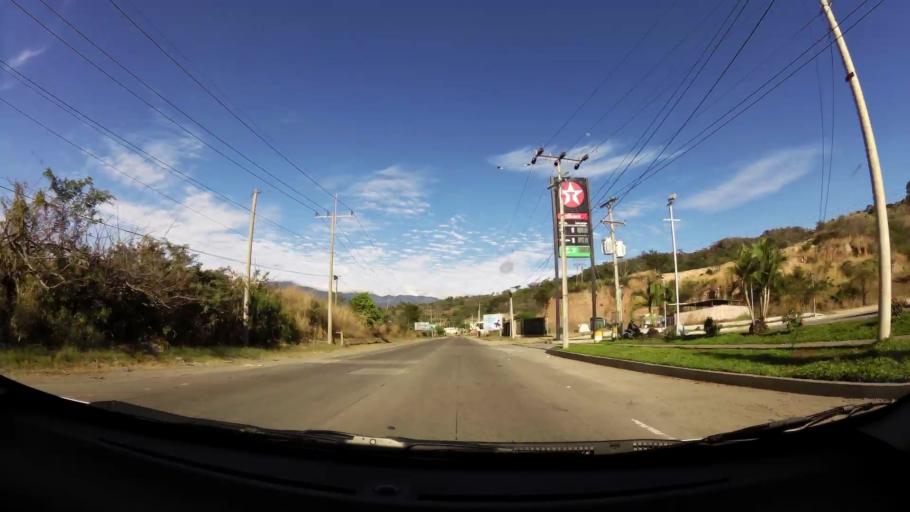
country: SV
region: Santa Ana
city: Metapan
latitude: 14.3035
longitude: -89.4574
